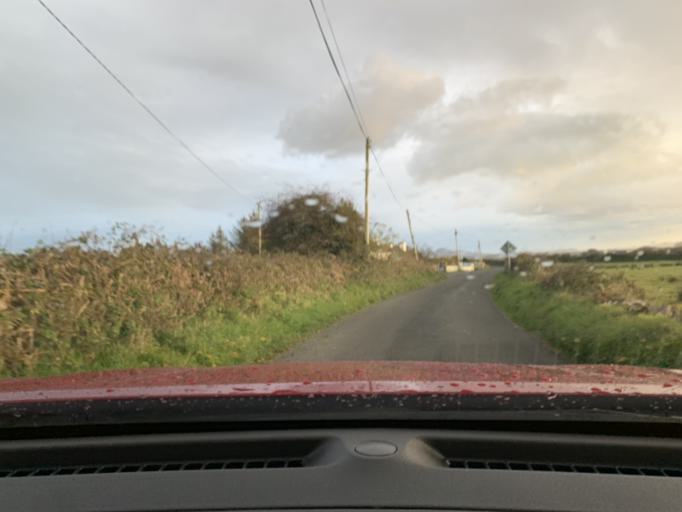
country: IE
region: Connaught
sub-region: Sligo
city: Sligo
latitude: 54.3086
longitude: -8.4997
